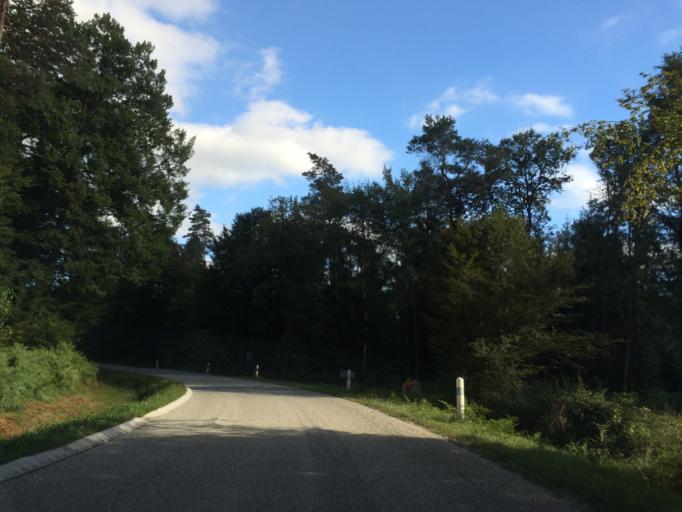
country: FR
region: Alsace
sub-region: Departement du Bas-Rhin
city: Soufflenheim
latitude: 48.8555
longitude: 7.9335
